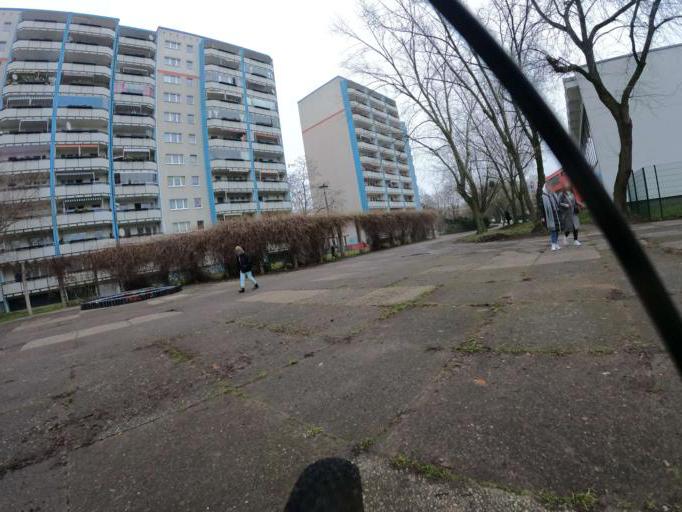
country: DE
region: Berlin
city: Marzahn
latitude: 52.5590
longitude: 13.5624
